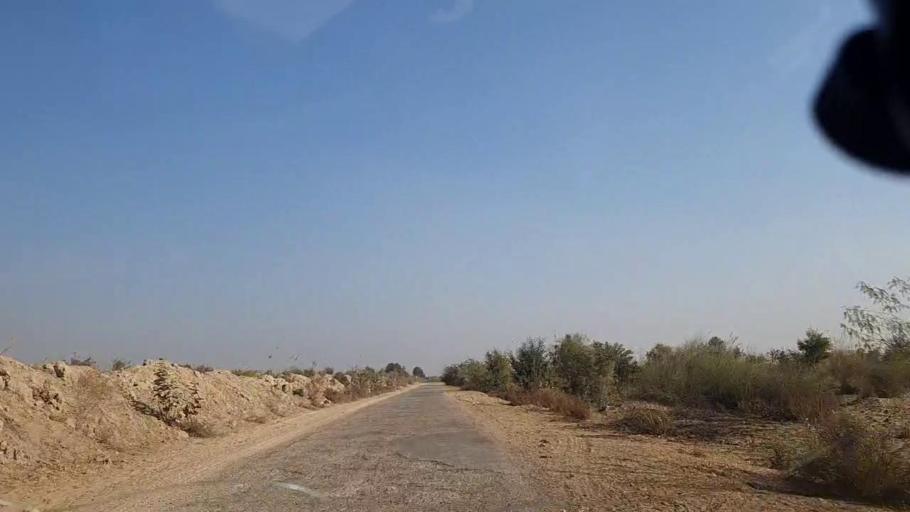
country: PK
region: Sindh
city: Khanpur
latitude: 27.6872
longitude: 69.5180
